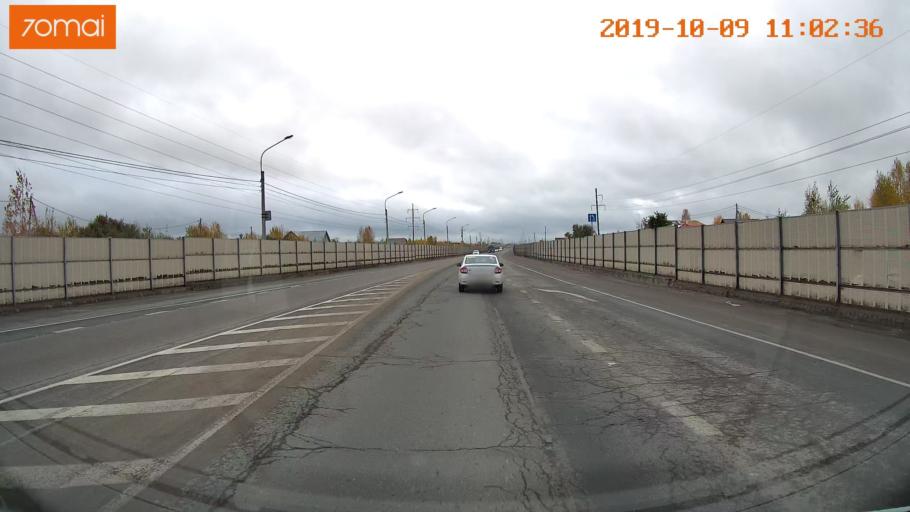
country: RU
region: Vologda
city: Vologda
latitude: 59.2296
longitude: 39.7744
